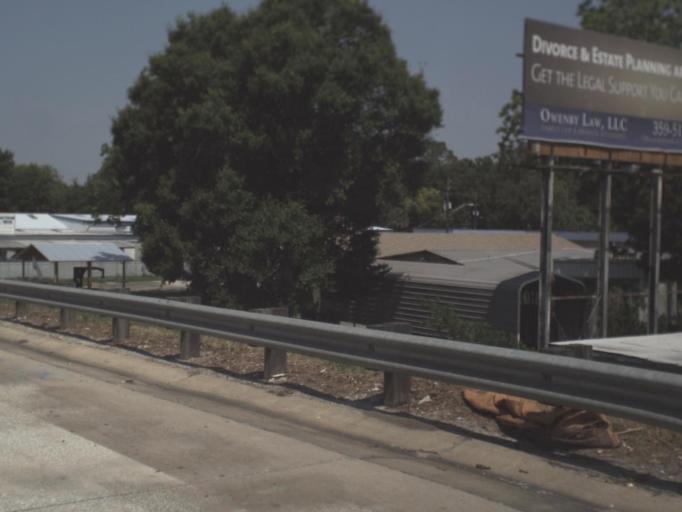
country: US
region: Florida
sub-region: Duval County
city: Jacksonville
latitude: 30.3209
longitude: -81.7141
